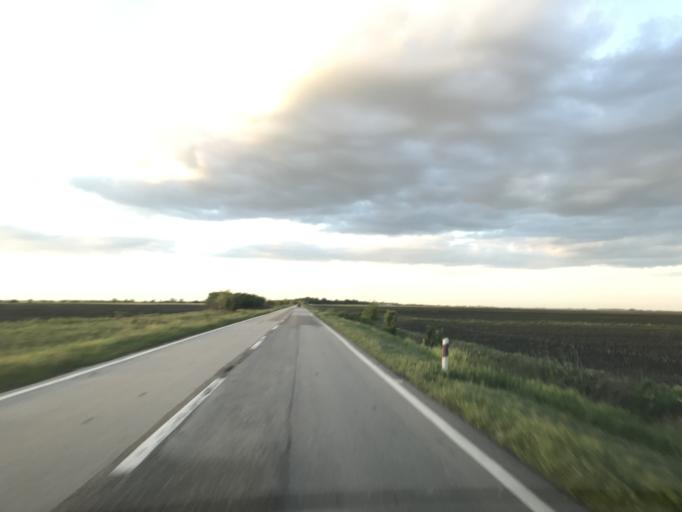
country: RS
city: Banatsko Karadordevo
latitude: 45.6020
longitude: 20.5650
